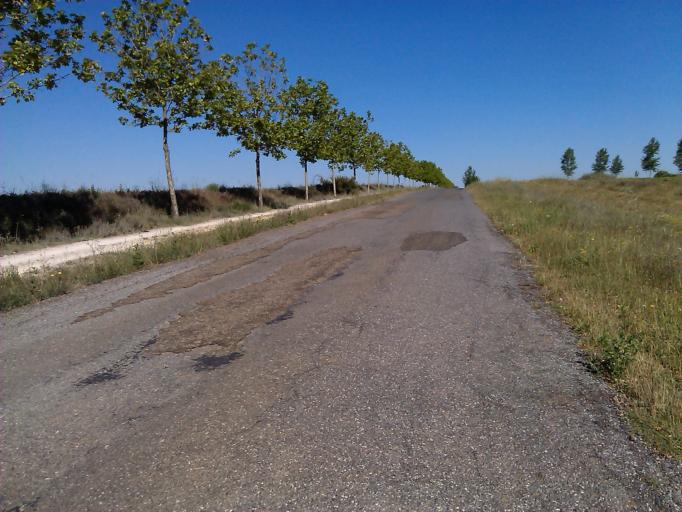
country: ES
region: Castille and Leon
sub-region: Provincia de Leon
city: Bercianos del Real Camino
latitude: 42.3997
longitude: -5.1712
